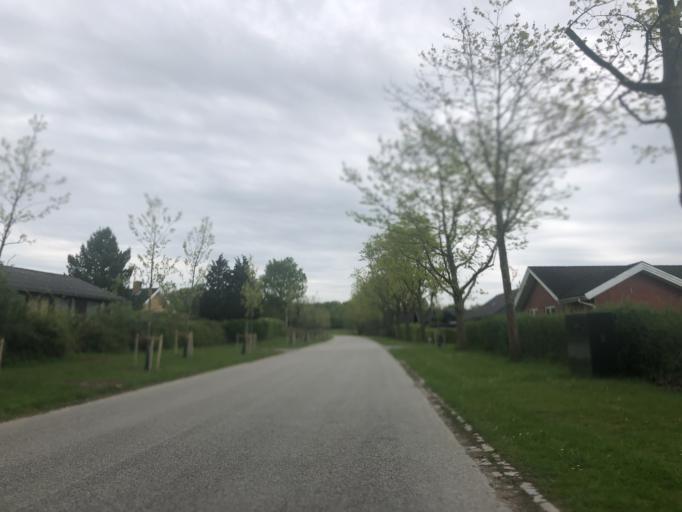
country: DK
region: Zealand
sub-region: Ringsted Kommune
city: Ringsted
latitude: 55.4460
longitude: 11.8207
